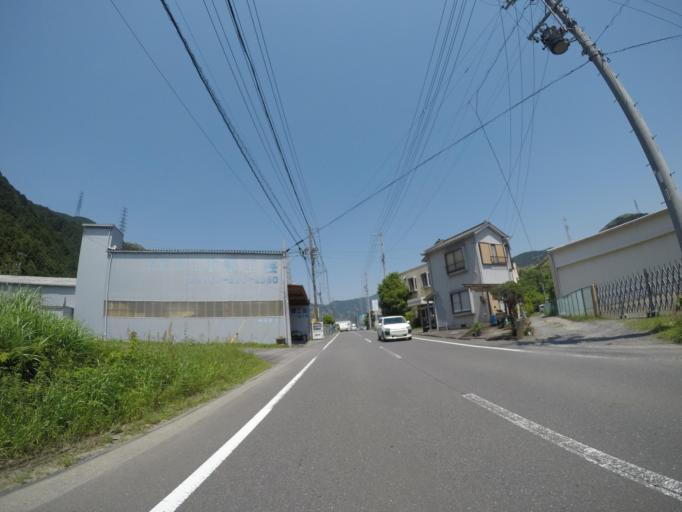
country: JP
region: Shizuoka
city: Shizuoka-shi
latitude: 34.9919
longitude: 138.2880
